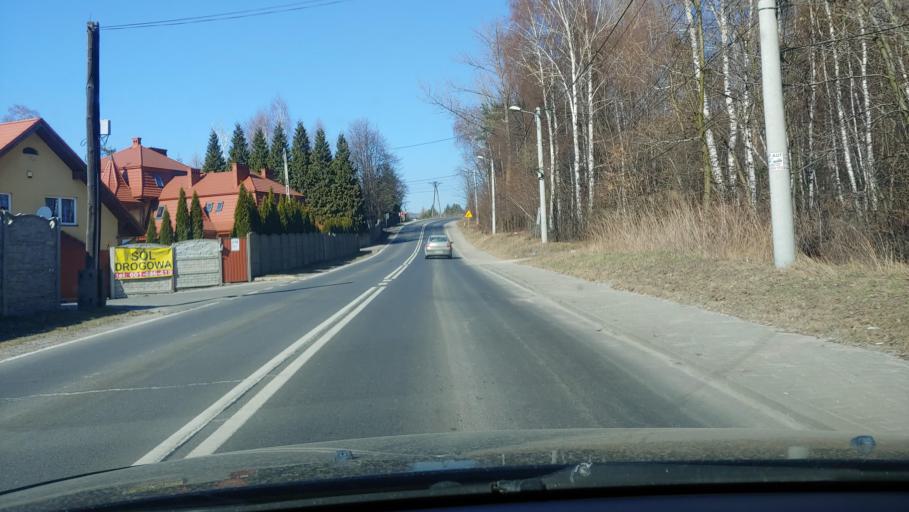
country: PL
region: Lesser Poland Voivodeship
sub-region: Powiat chrzanowski
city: Myslachowice
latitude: 50.1752
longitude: 19.4735
